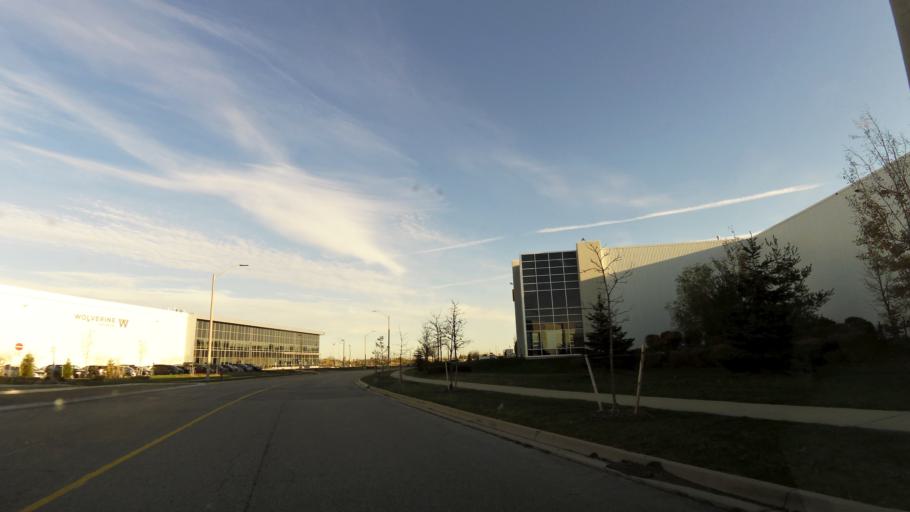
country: CA
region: Ontario
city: Mississauga
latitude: 43.5884
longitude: -79.7334
